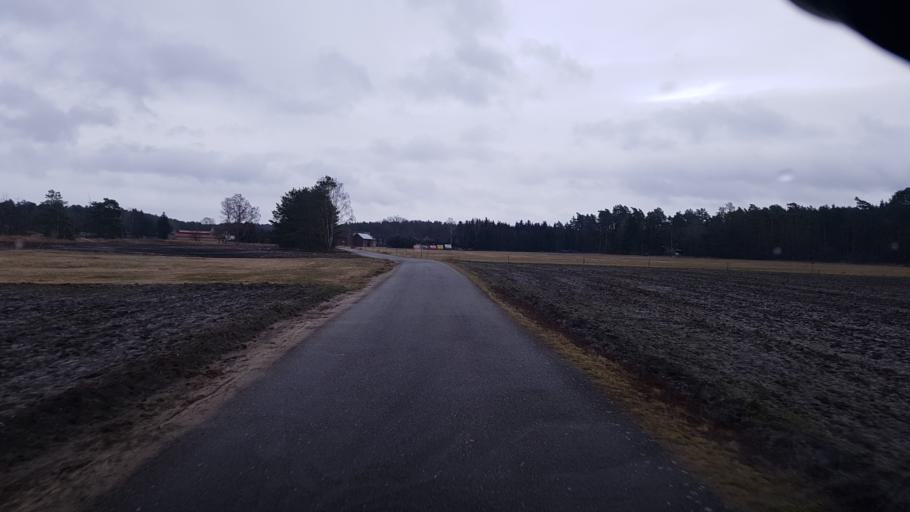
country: DE
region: Brandenburg
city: Sallgast
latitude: 51.6658
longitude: 13.8190
